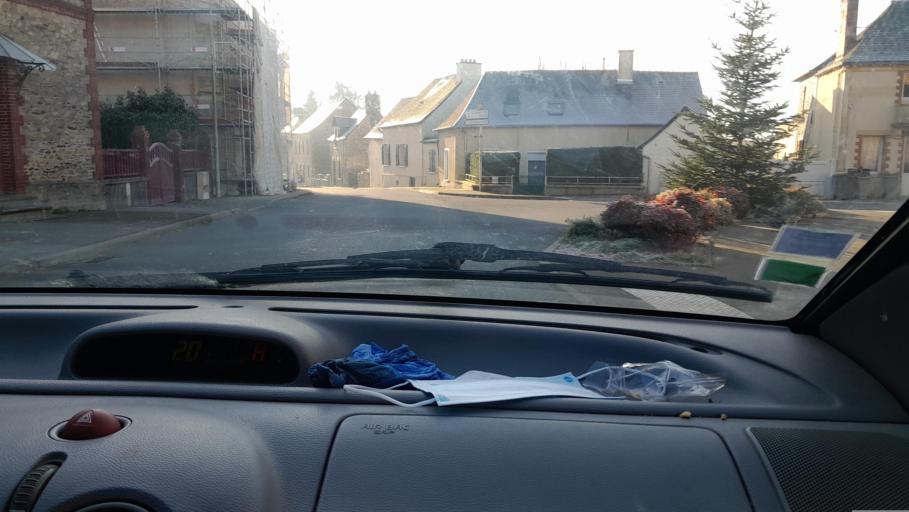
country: FR
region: Brittany
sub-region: Departement d'Ille-et-Vilaine
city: Rannee
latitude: 47.8866
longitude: -1.1817
